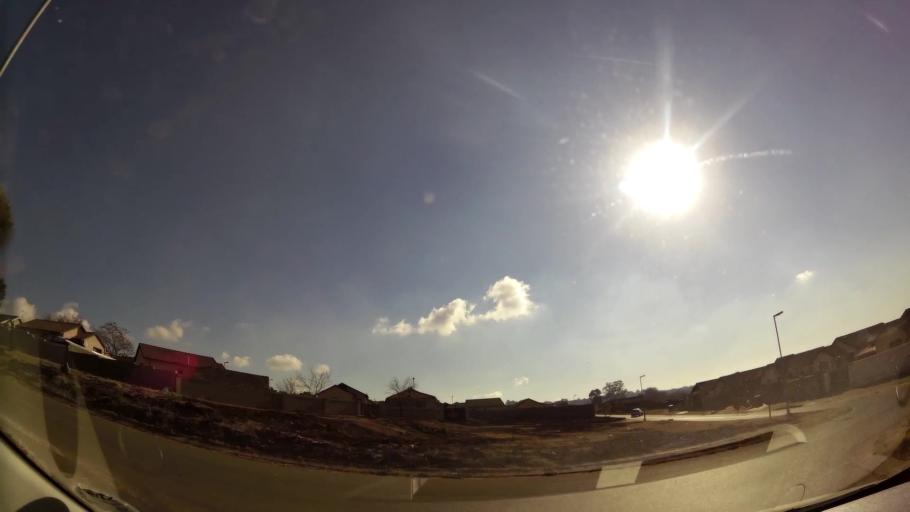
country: ZA
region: Gauteng
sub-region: City of Johannesburg Metropolitan Municipality
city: Roodepoort
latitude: -26.1623
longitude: 27.8342
